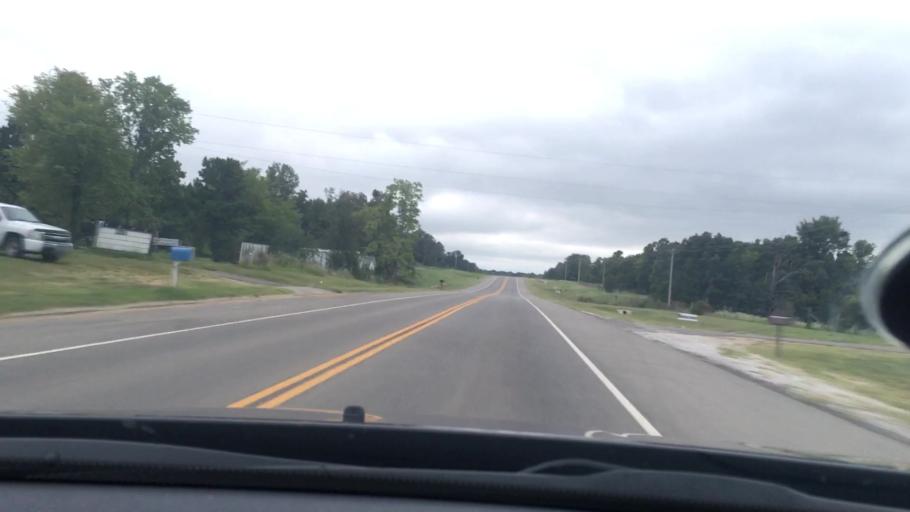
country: US
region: Oklahoma
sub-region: Sequoyah County
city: Vian
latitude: 35.6040
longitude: -94.9763
